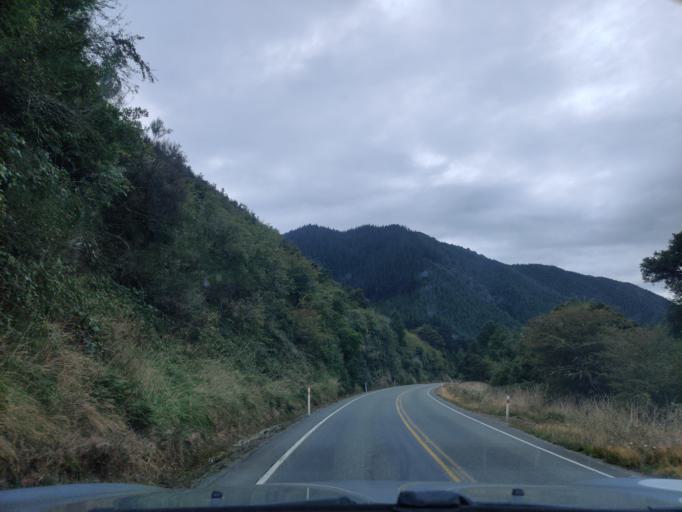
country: NZ
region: Tasman
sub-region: Tasman District
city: Wakefield
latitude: -41.6974
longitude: 172.6333
